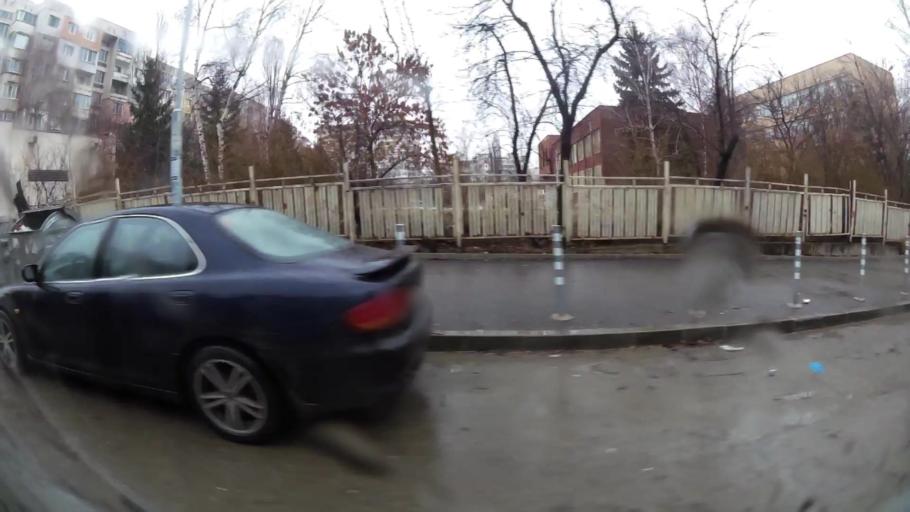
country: BG
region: Sofia-Capital
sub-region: Stolichna Obshtina
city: Sofia
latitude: 42.6428
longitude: 23.3724
